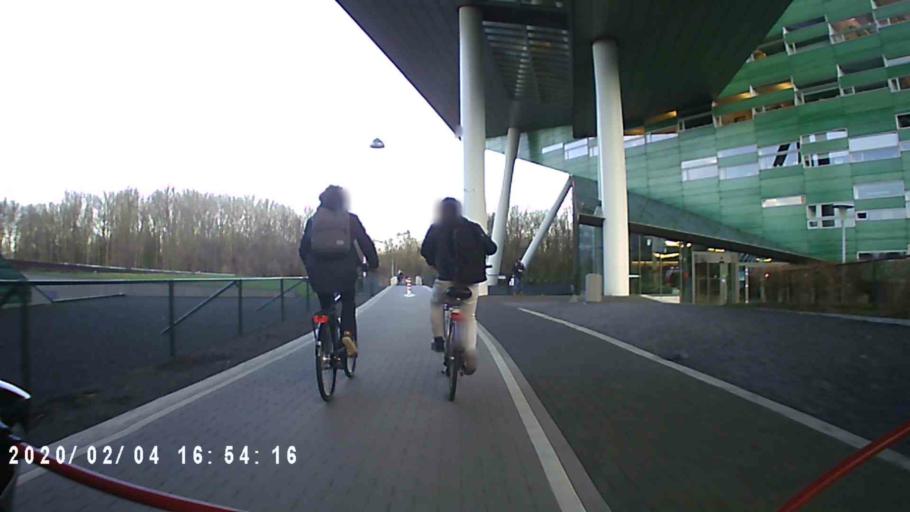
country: NL
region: Groningen
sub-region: Gemeente Groningen
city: Korrewegwijk
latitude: 53.2412
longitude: 6.5381
